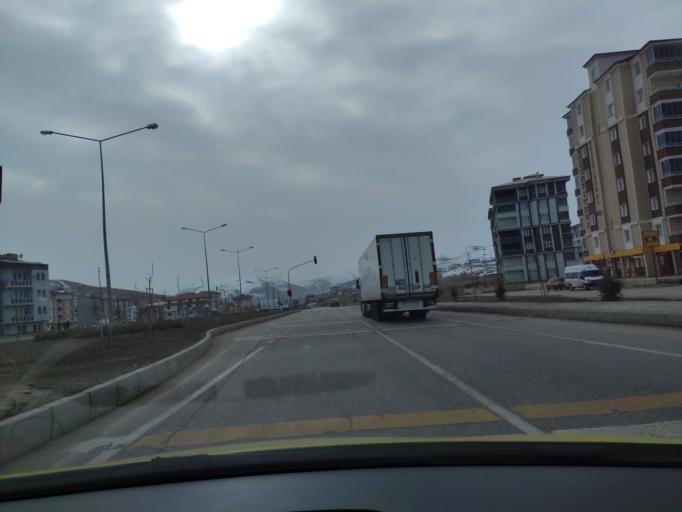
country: TR
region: Bayburt
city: Bayburt
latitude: 40.2659
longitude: 40.2032
